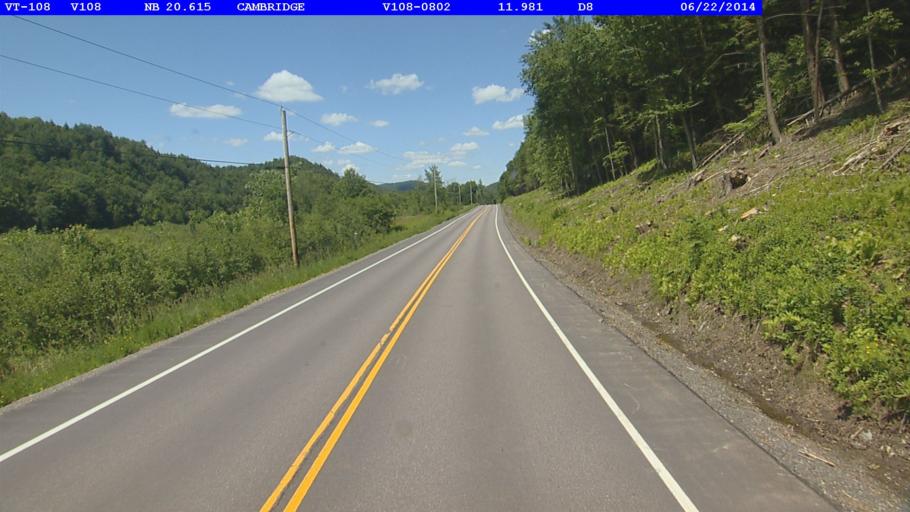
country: US
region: Vermont
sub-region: Lamoille County
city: Johnson
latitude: 44.6878
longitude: -72.8263
